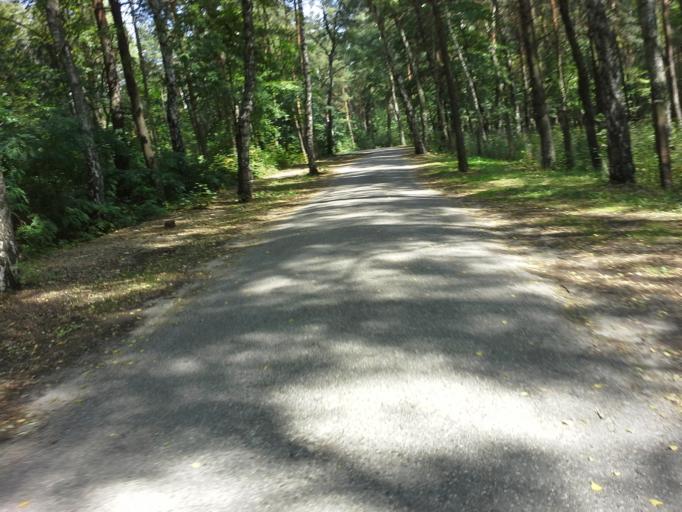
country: PL
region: Lesser Poland Voivodeship
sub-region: Powiat chrzanowski
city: Trzebinia
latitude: 50.1398
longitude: 19.4507
